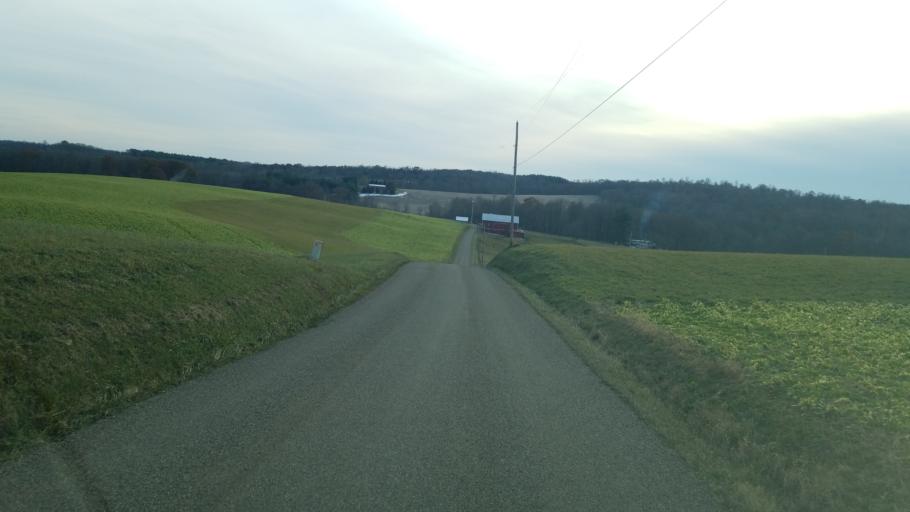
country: US
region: Ohio
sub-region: Sandusky County
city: Bellville
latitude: 40.6511
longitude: -82.4270
